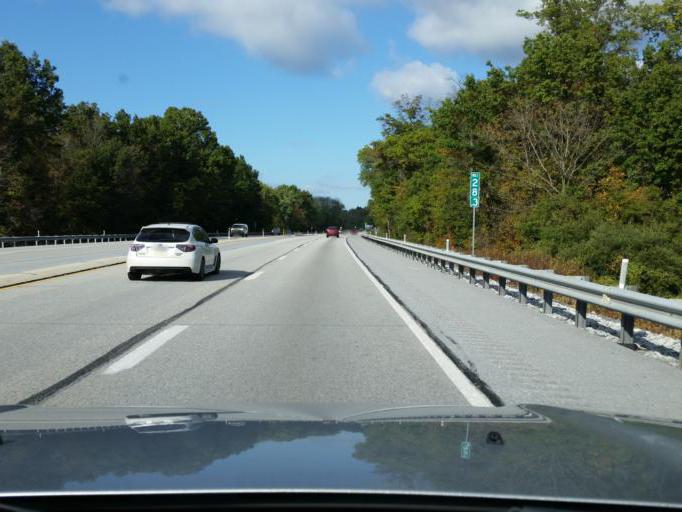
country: US
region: Pennsylvania
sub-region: York County
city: Dillsburg
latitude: 40.0604
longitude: -77.0658
